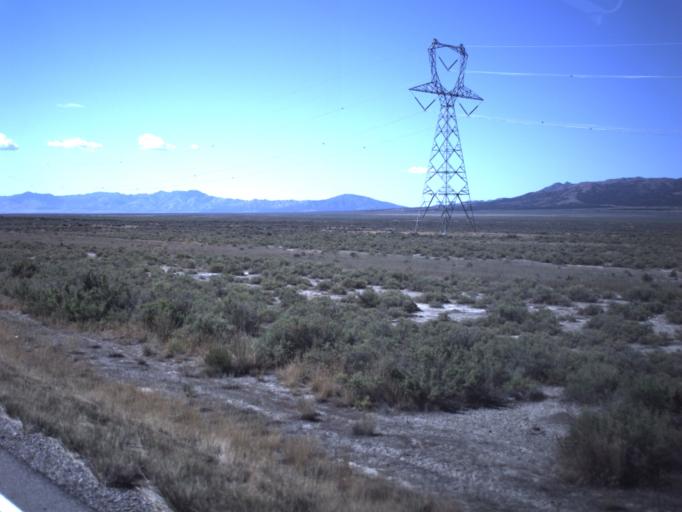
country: US
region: Utah
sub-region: Tooele County
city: Tooele
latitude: 40.2920
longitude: -112.4009
